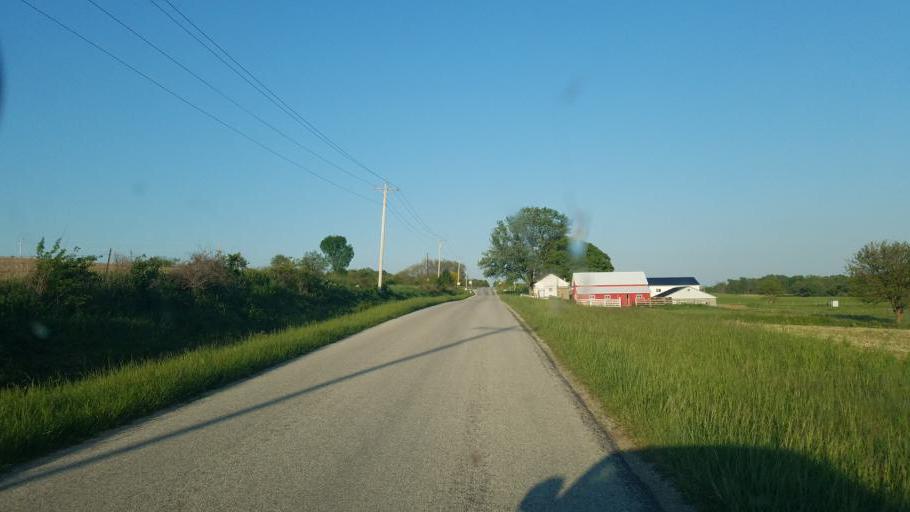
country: US
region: Ohio
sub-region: Morrow County
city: Mount Gilead
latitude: 40.5216
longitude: -82.7137
